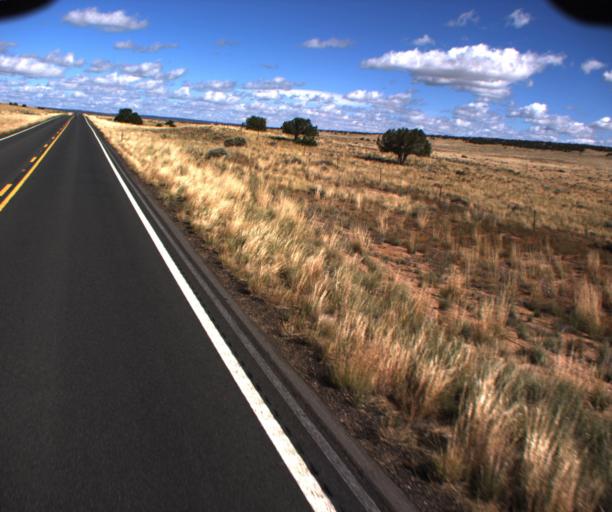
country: US
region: Arizona
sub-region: Apache County
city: Houck
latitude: 34.9679
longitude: -109.2274
